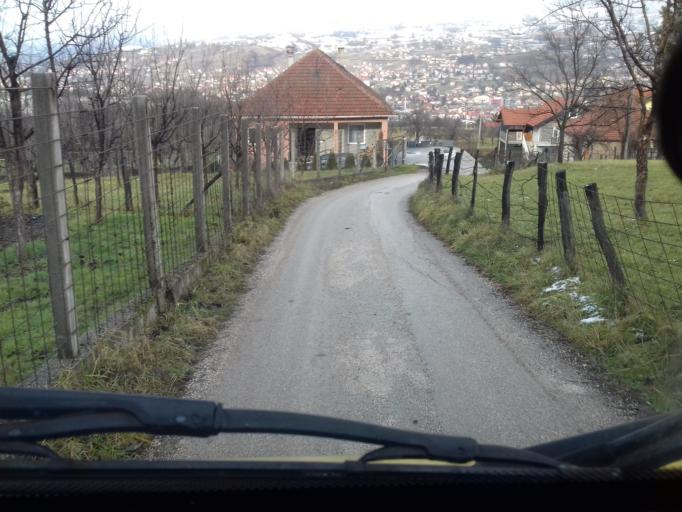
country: BA
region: Federation of Bosnia and Herzegovina
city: Zenica
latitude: 44.1806
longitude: 17.9453
